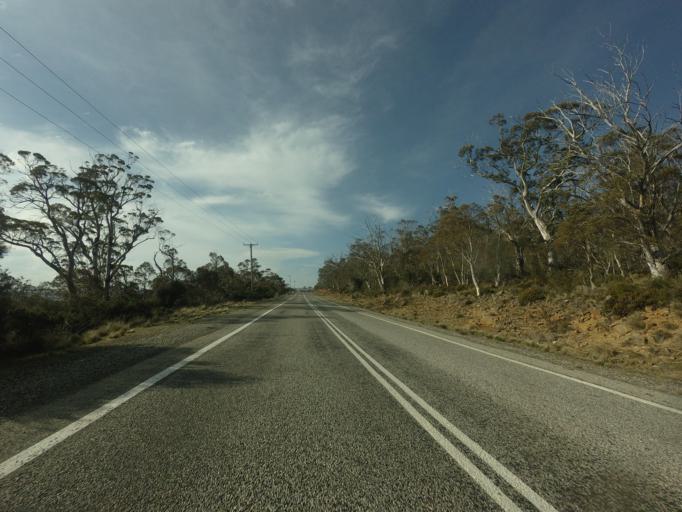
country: AU
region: Tasmania
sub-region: Meander Valley
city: Deloraine
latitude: -41.9861
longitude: 146.7118
